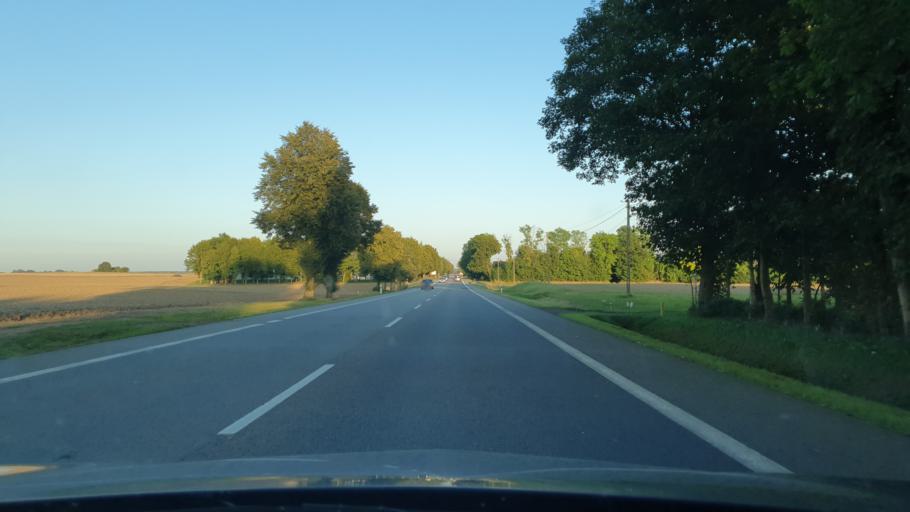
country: PL
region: Pomeranian Voivodeship
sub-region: Powiat slupski
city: Debnica Kaszubska
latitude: 54.4671
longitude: 17.1696
